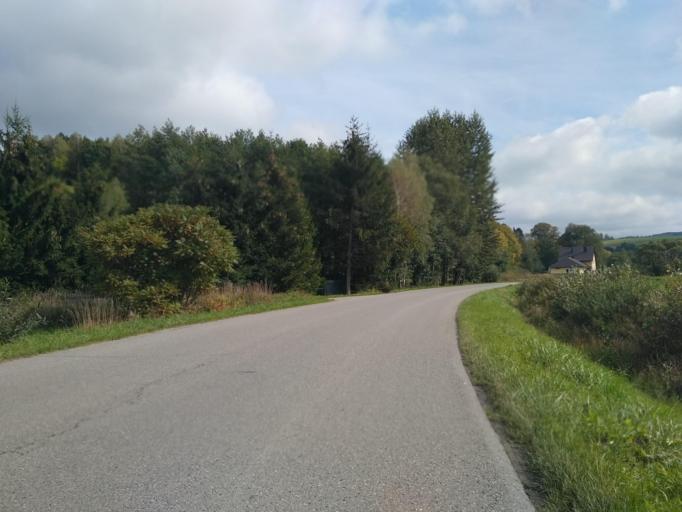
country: PL
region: Subcarpathian Voivodeship
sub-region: Powiat ropczycko-sedziszowski
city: Niedzwiada
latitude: 49.9330
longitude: 21.5500
